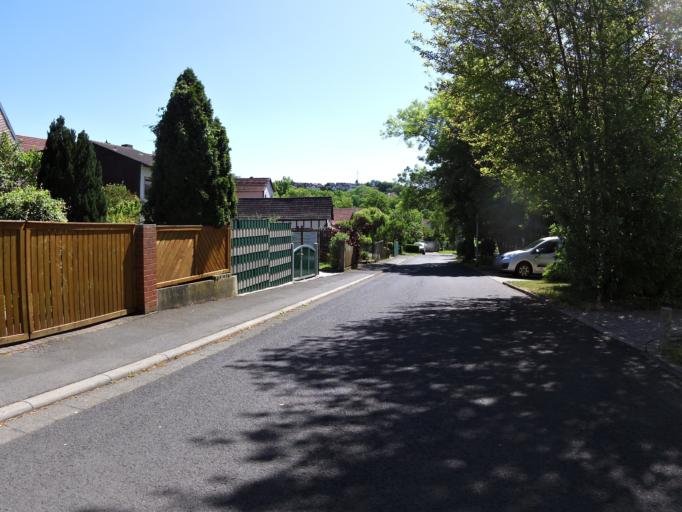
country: DE
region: Hesse
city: Philippsthal
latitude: 50.8417
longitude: 10.0038
